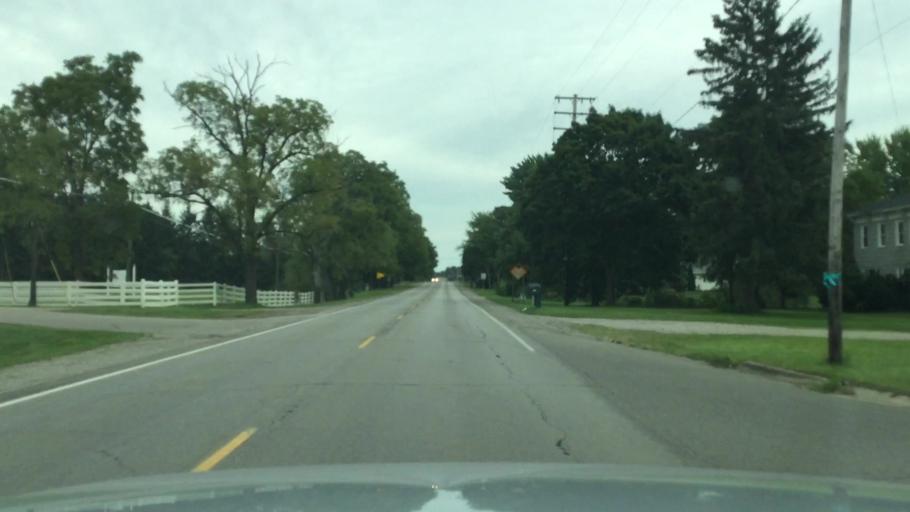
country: US
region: Michigan
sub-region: Genesee County
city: Swartz Creek
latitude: 42.9570
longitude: -83.8654
